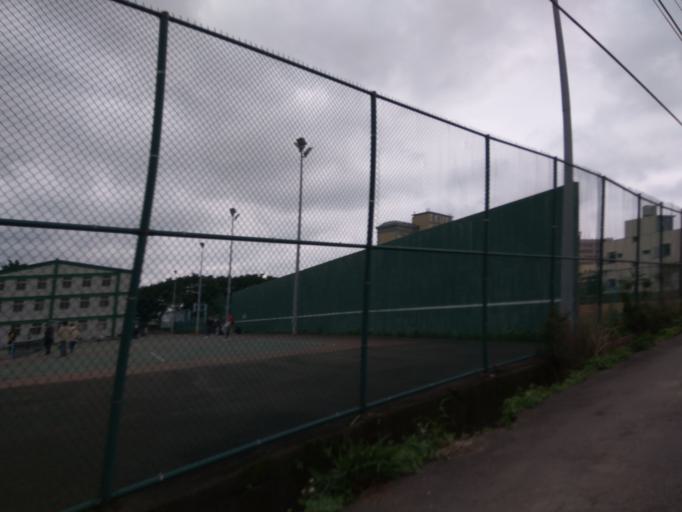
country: TW
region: Taiwan
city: Taoyuan City
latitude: 24.9936
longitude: 121.2272
